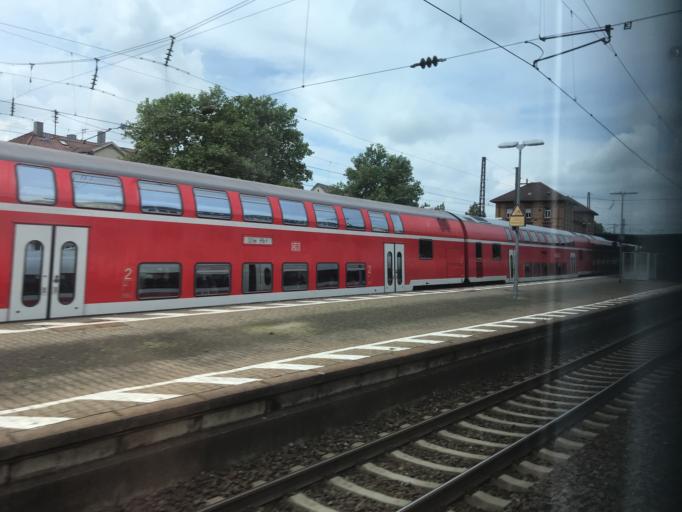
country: DE
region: Baden-Wuerttemberg
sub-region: Regierungsbezirk Stuttgart
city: Sussen
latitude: 48.6832
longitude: 9.7614
